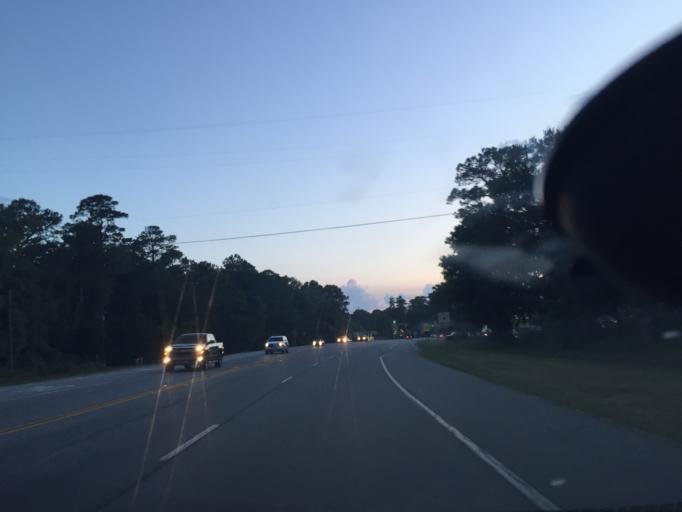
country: US
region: Georgia
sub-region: Chatham County
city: Wilmington Island
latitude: 32.0332
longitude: -80.9619
